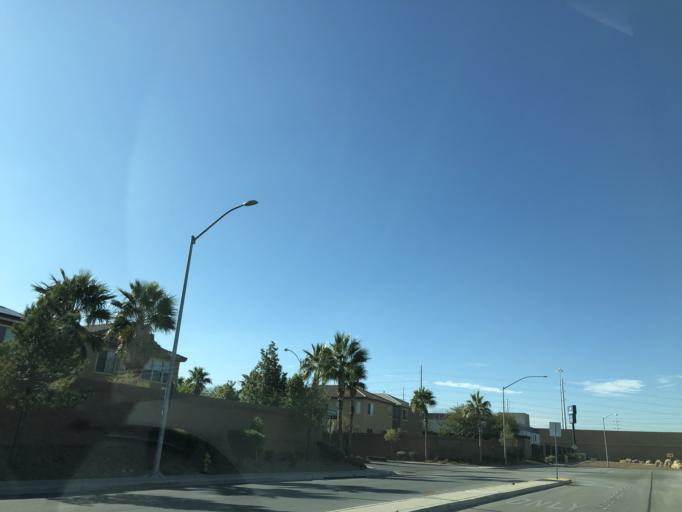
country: US
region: Nevada
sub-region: Clark County
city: Whitney
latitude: 36.0709
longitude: -115.0333
